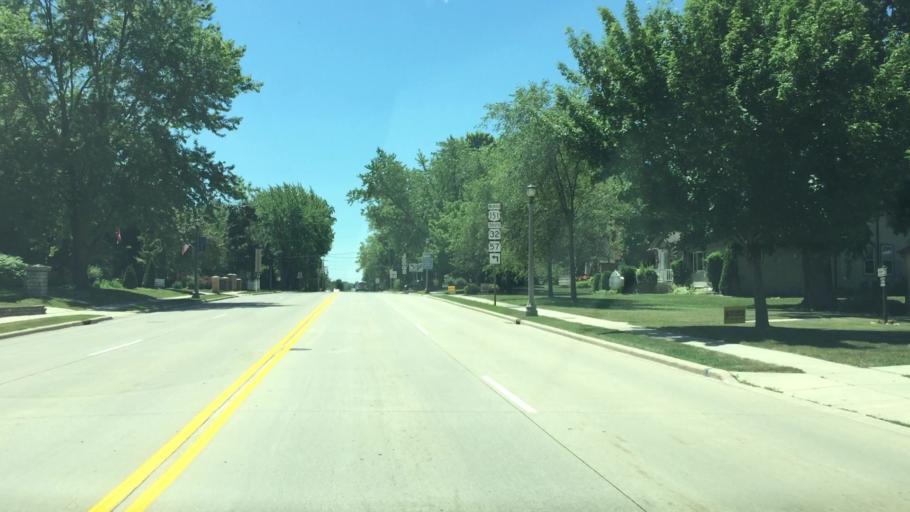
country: US
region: Wisconsin
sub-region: Calumet County
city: Chilton
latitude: 44.0253
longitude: -88.1628
